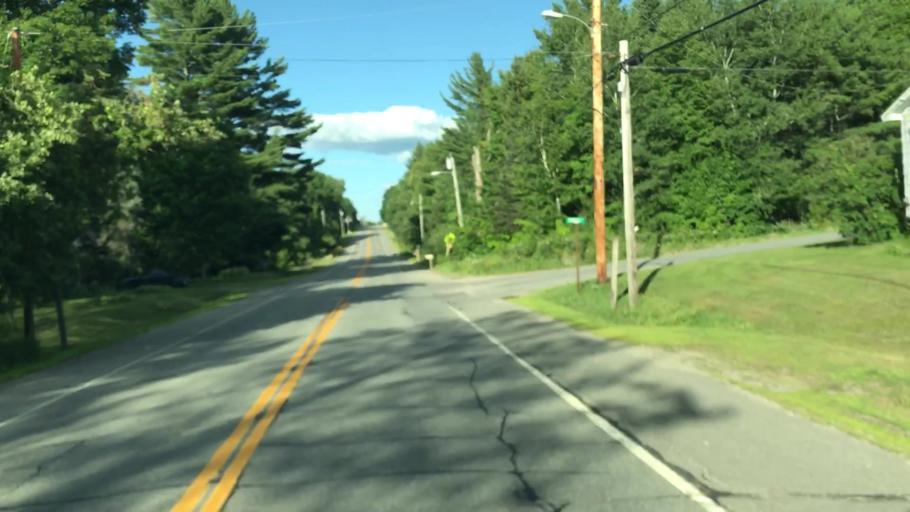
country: US
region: Maine
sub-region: Penobscot County
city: Lincoln
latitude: 45.3591
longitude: -68.2789
